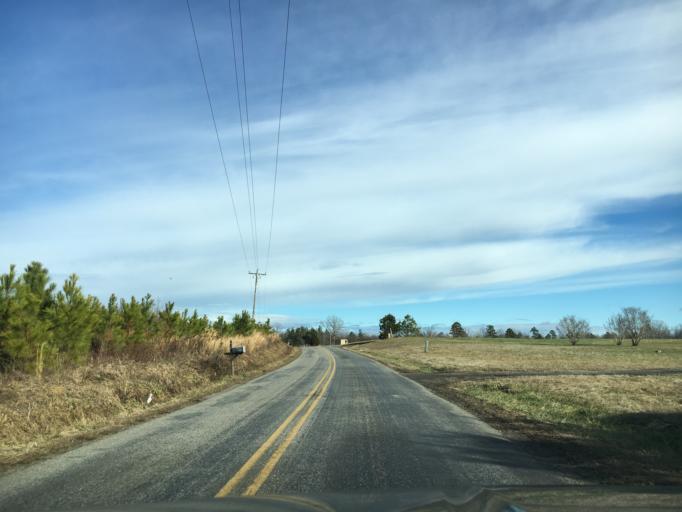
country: US
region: Virginia
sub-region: Nottoway County
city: Crewe
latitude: 37.3296
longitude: -78.1642
